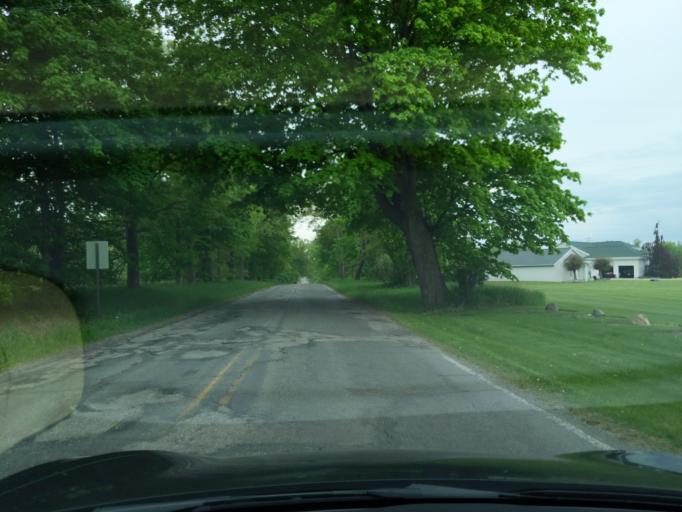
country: US
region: Michigan
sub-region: Ingham County
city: Leslie
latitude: 42.3869
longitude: -84.3296
